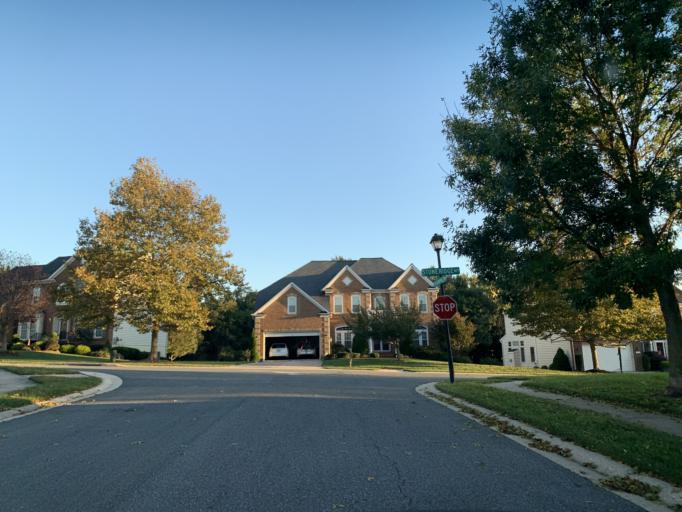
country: US
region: Maryland
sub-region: Harford County
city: Bel Air South
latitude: 39.5258
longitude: -76.2990
